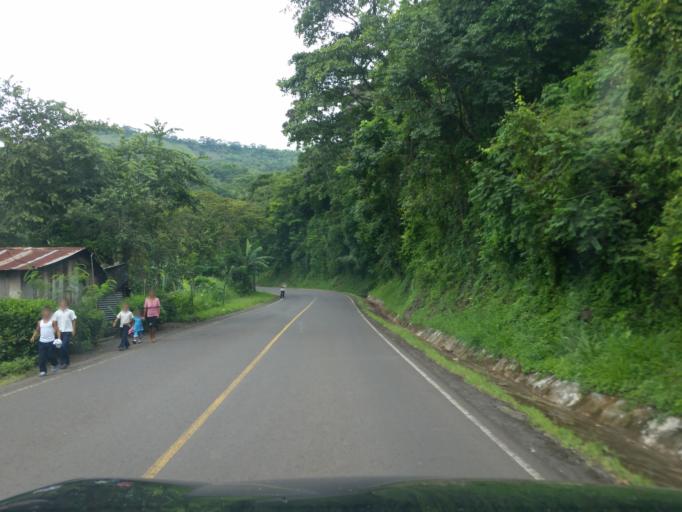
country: NI
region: Matagalpa
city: San Ramon
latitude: 12.9980
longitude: -85.8167
